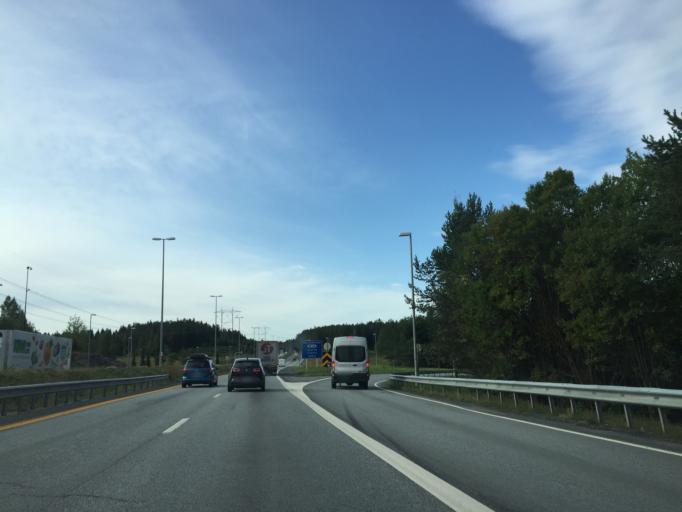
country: NO
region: Akershus
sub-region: Oppegard
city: Kolbotn
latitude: 59.7968
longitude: 10.8425
